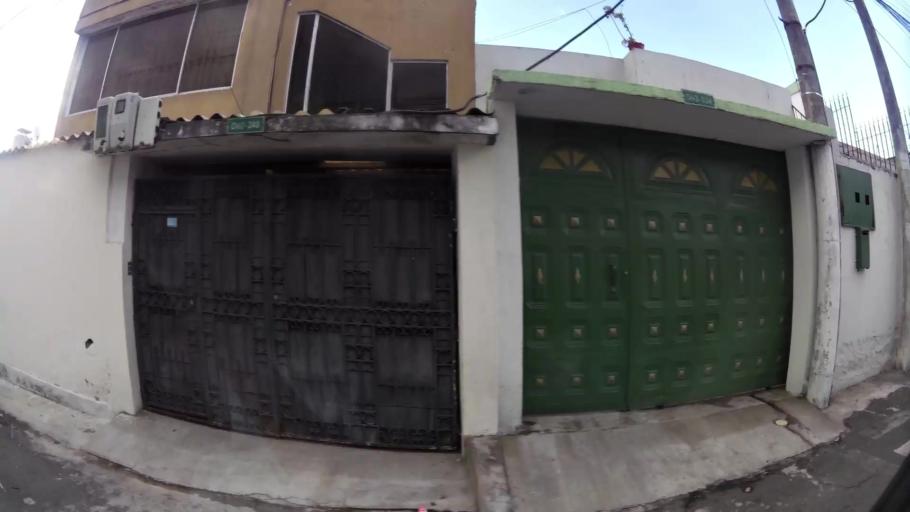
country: EC
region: Pichincha
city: Quito
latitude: -0.1256
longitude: -78.4889
